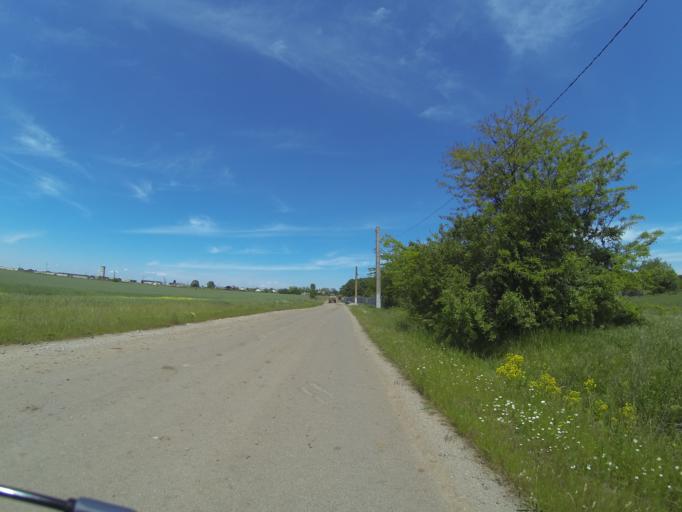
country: RO
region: Dolj
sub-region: Comuna Teslui
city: Teslui
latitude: 44.1667
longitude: 24.1606
